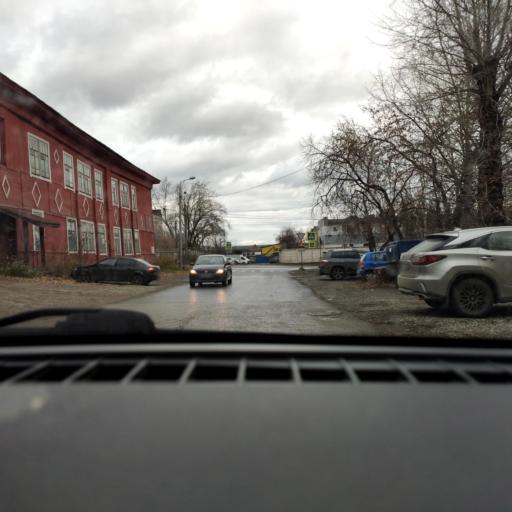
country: RU
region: Perm
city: Perm
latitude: 58.0079
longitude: 56.1802
